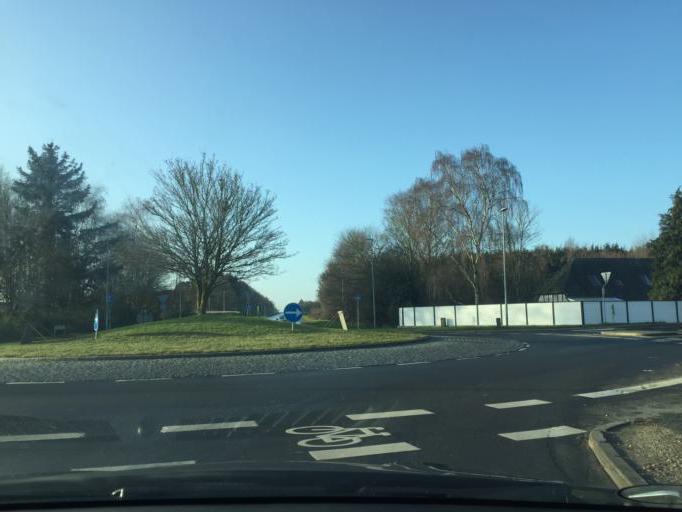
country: DK
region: South Denmark
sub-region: Faaborg-Midtfyn Kommune
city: Faaborg
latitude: 55.1088
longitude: 10.2249
